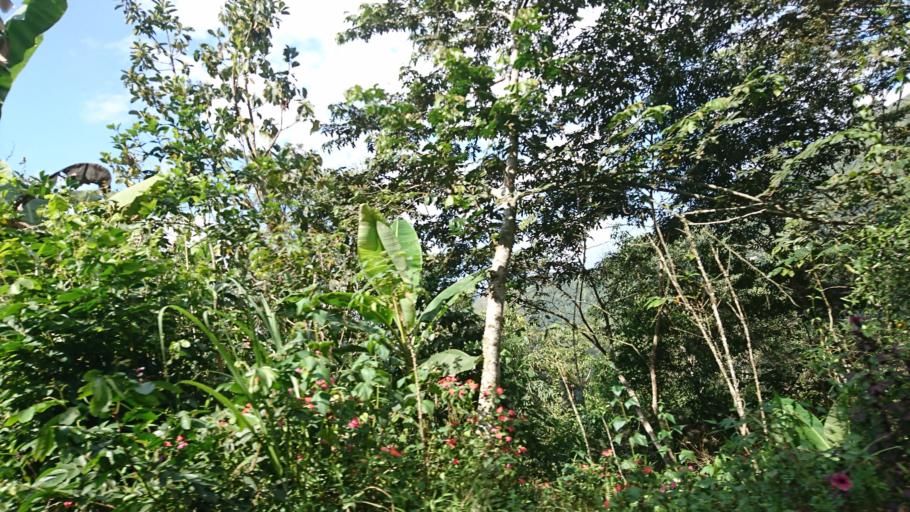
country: BO
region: La Paz
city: Coroico
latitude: -16.0764
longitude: -67.7884
